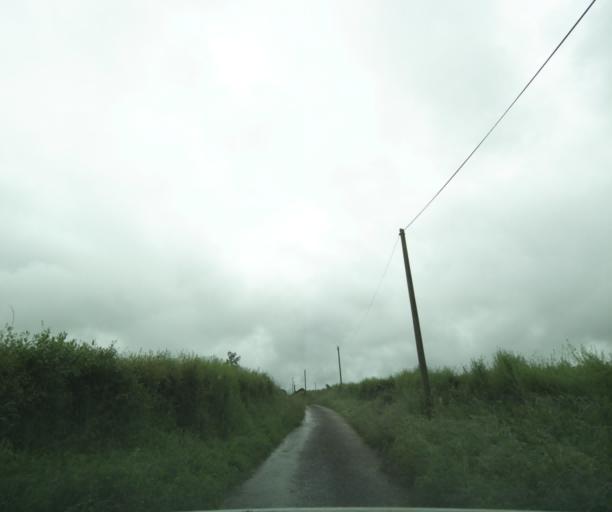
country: FR
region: Bourgogne
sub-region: Departement de Saone-et-Loire
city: Charolles
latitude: 46.4644
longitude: 4.3145
